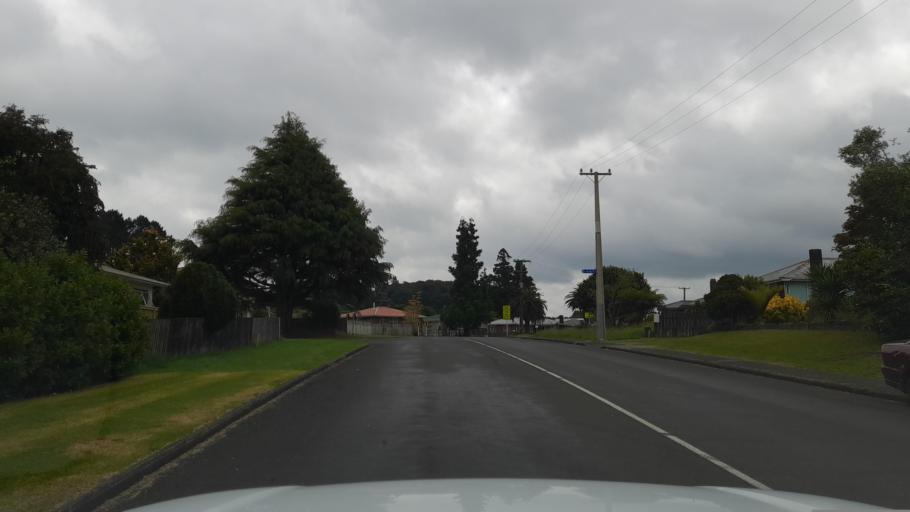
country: NZ
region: Northland
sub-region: Far North District
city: Waimate North
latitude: -35.4092
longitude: 173.7924
